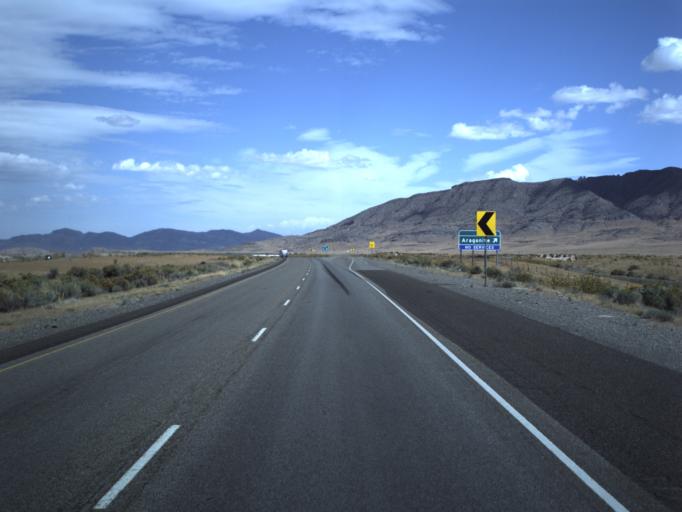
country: US
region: Utah
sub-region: Tooele County
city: Grantsville
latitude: 40.7653
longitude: -112.9912
